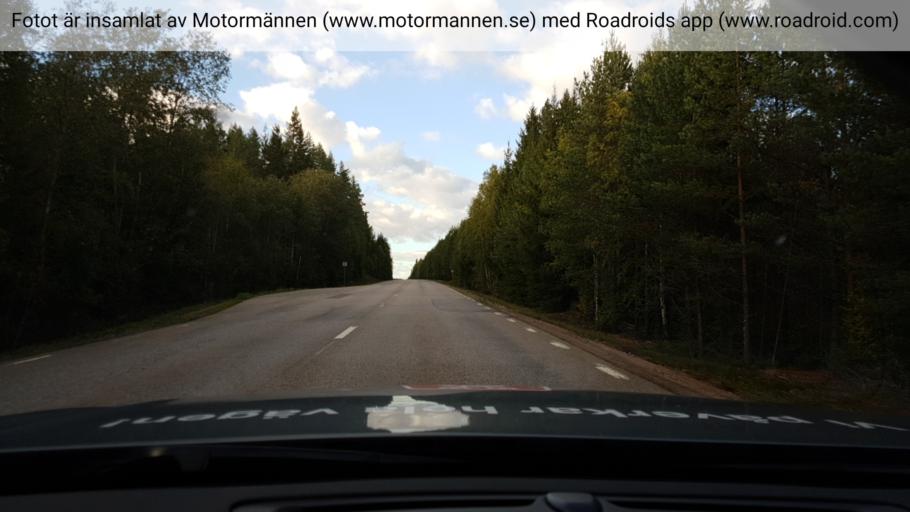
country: SE
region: Vaermland
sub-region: Filipstads Kommun
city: Lesjofors
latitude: 59.9030
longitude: 14.0016
